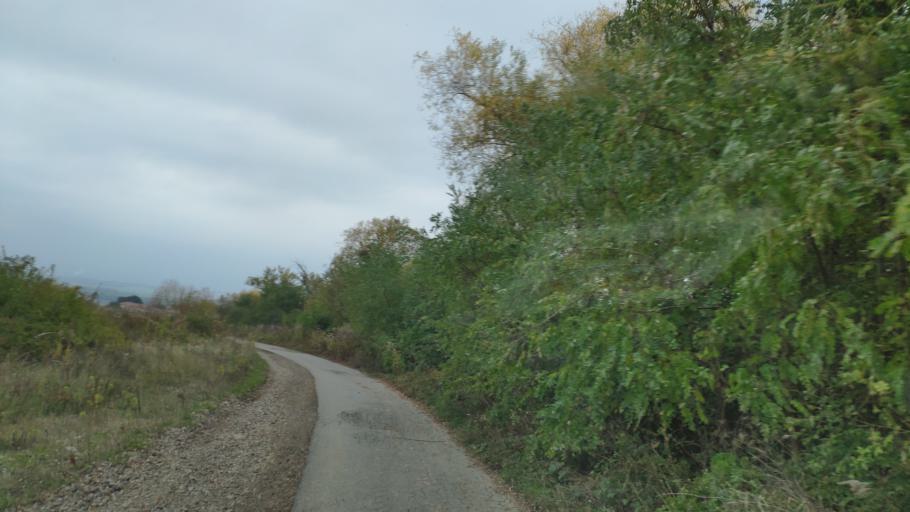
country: SK
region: Kosicky
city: Kosice
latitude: 48.6319
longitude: 21.3985
